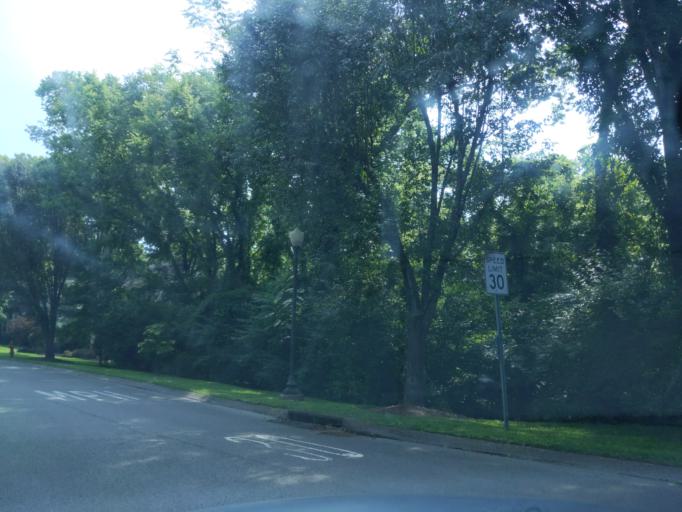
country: US
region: Tennessee
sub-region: Williamson County
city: Brentwood Estates
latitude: 36.0278
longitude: -86.7527
